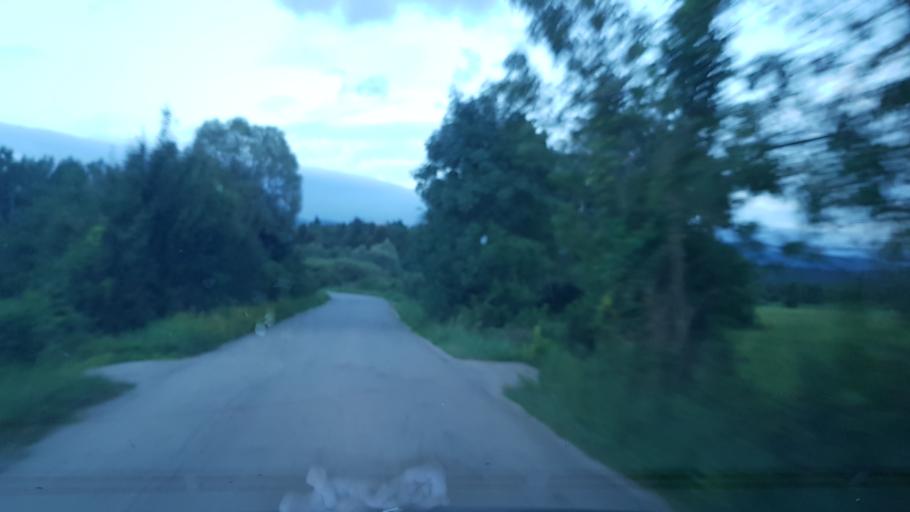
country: SI
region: Postojna
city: Postojna
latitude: 45.7537
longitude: 14.1846
